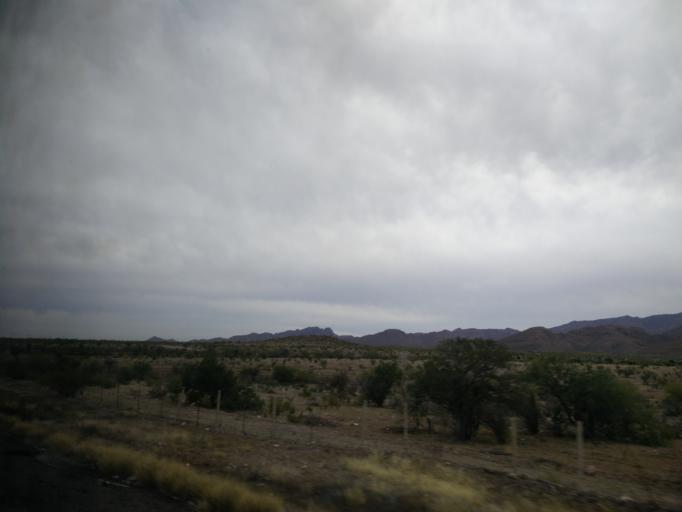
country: MX
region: Sonora
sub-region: Hermosillo
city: Miguel Aleman (La Doce)
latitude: 28.5213
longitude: -111.0464
